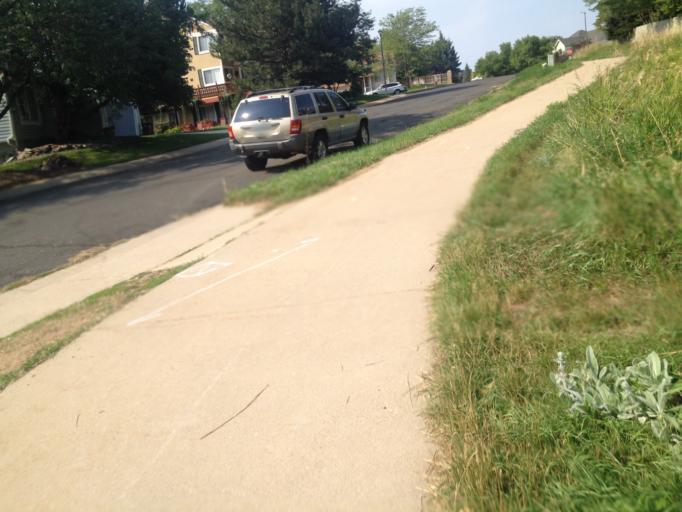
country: US
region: Colorado
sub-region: Boulder County
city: Superior
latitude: 39.9763
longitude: -105.1620
